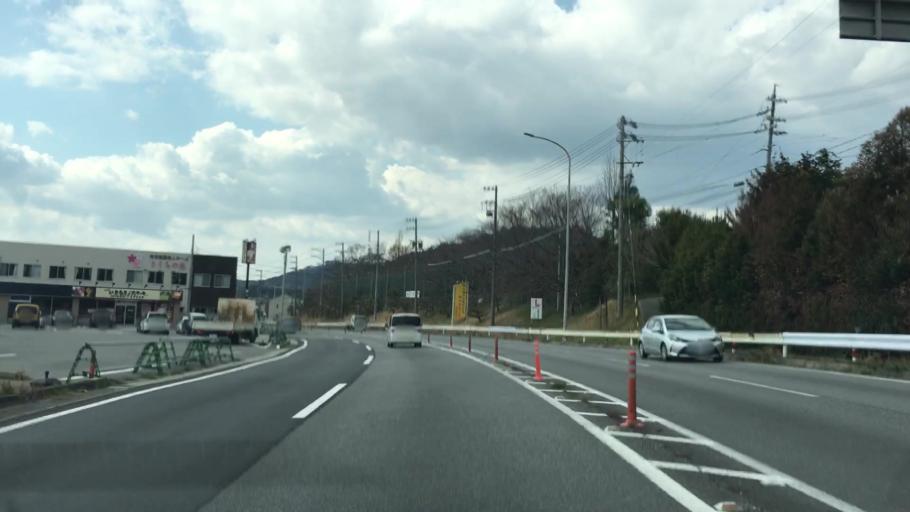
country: JP
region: Aichi
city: Gamagori
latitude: 34.8125
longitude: 137.2935
